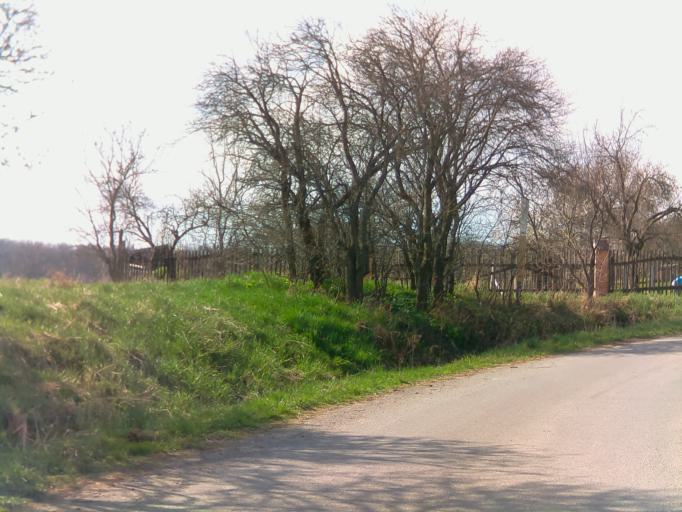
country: DE
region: Thuringia
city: Milda
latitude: 50.8476
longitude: 11.4866
